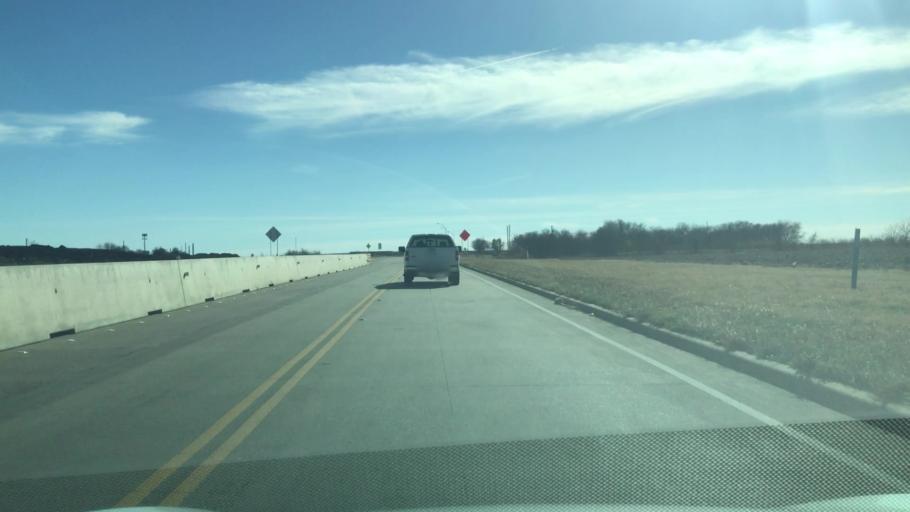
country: US
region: Texas
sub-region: Tarrant County
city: Mansfield
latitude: 32.5331
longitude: -97.0823
